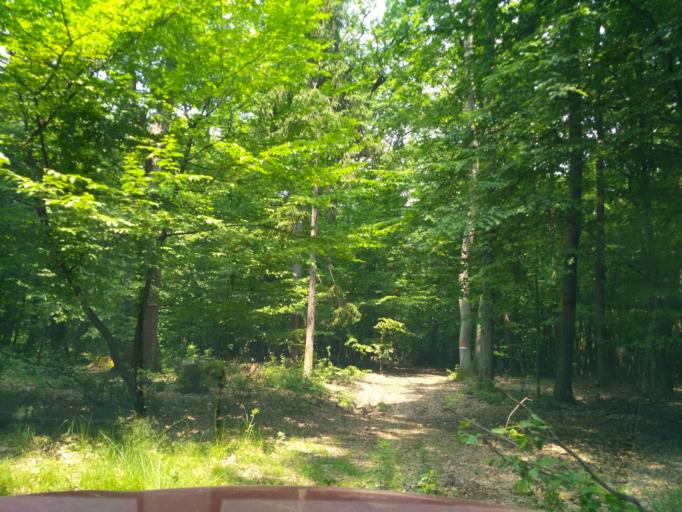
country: SK
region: Kosicky
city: Moldava nad Bodvou
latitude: 48.6548
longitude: 21.0342
